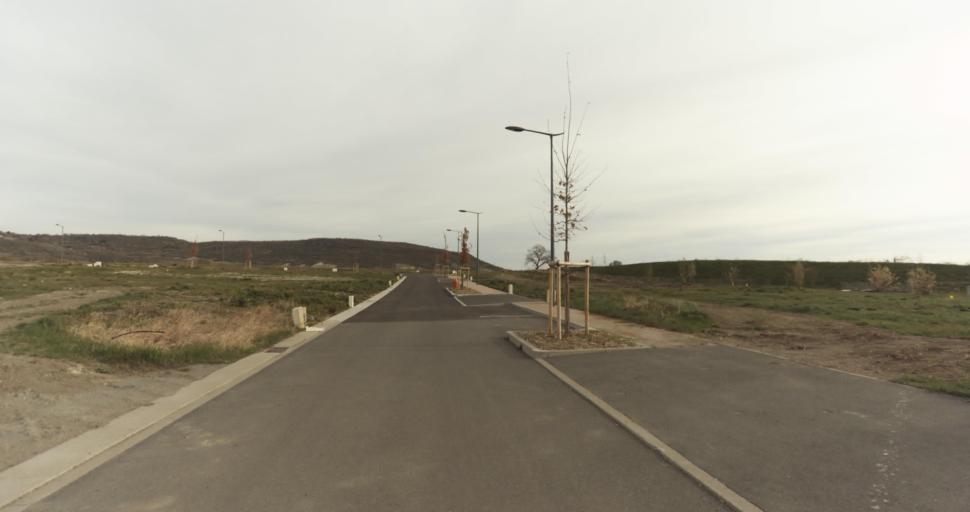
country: FR
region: Auvergne
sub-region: Departement du Puy-de-Dome
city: Cebazat
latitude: 45.8406
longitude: 3.1097
